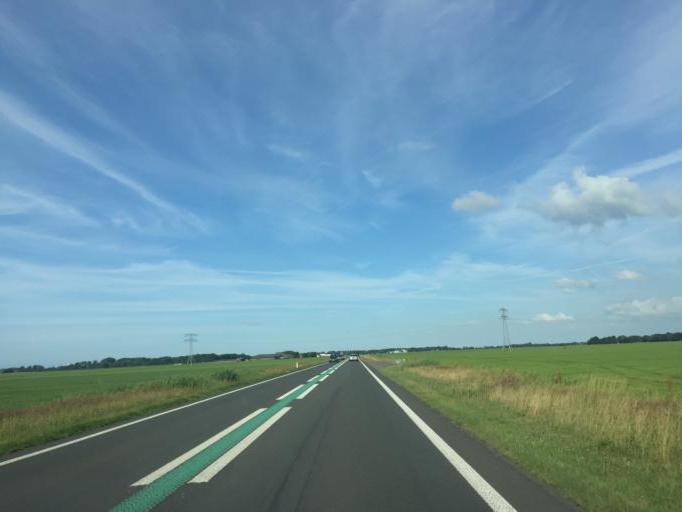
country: NL
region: Friesland
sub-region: Gemeente Dantumadiel
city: Rinsumageast
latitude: 53.3042
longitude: 5.9574
